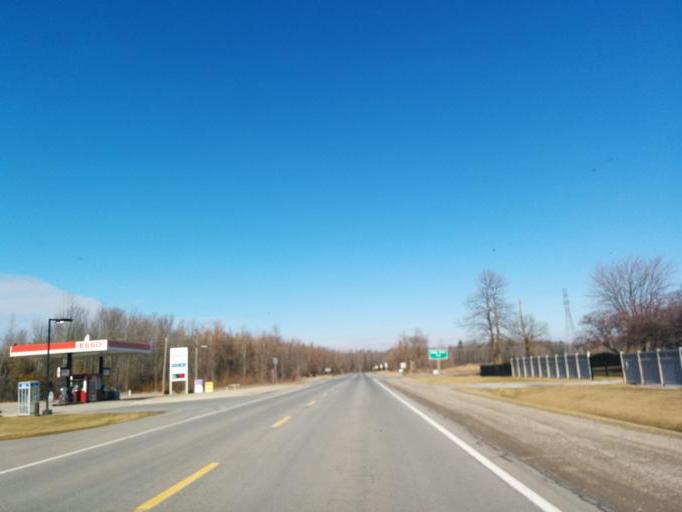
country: CA
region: Ontario
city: Brant
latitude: 43.0509
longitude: -80.3686
